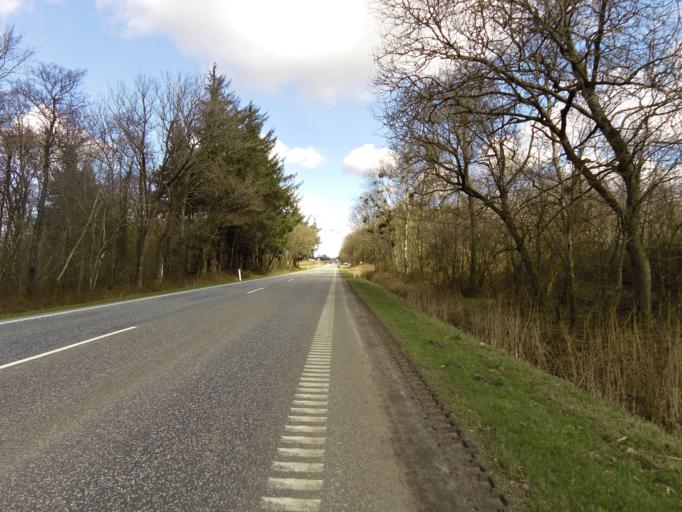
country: DK
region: South Denmark
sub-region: Tonder Kommune
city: Toftlund
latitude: 55.1731
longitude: 9.0557
